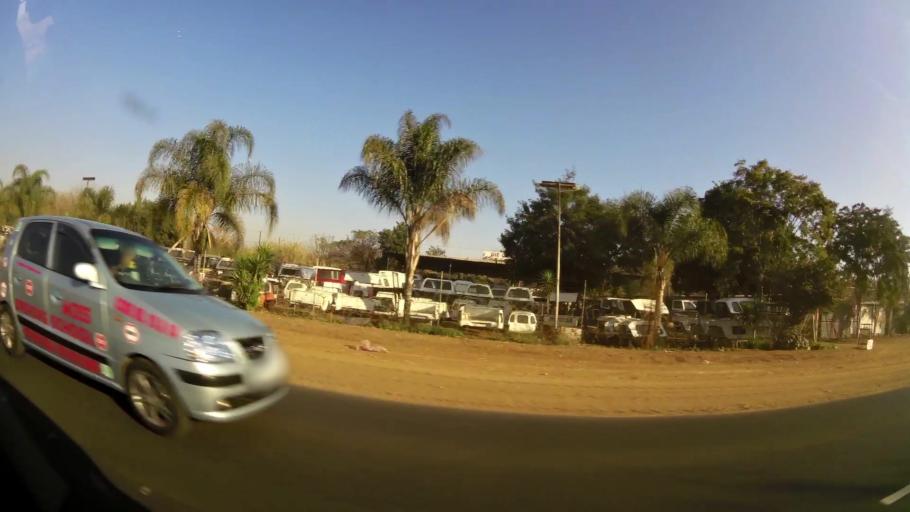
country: ZA
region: Gauteng
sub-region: City of Tshwane Metropolitan Municipality
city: Pretoria
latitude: -25.6307
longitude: 28.2020
